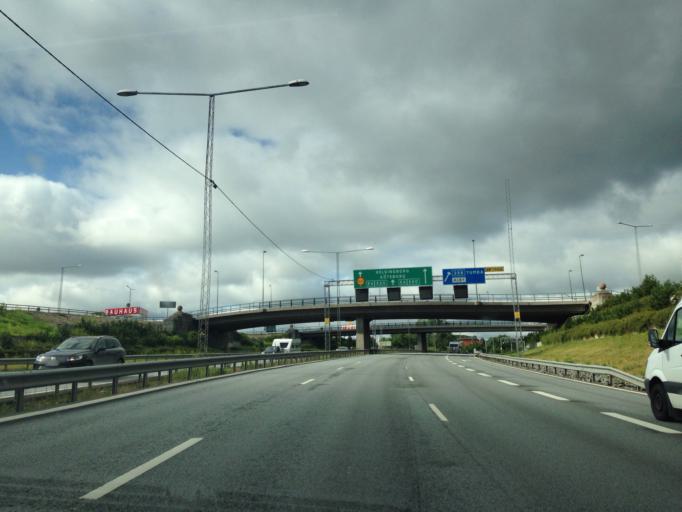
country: SE
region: Stockholm
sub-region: Botkyrka Kommun
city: Alby
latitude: 59.2412
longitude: 17.8362
